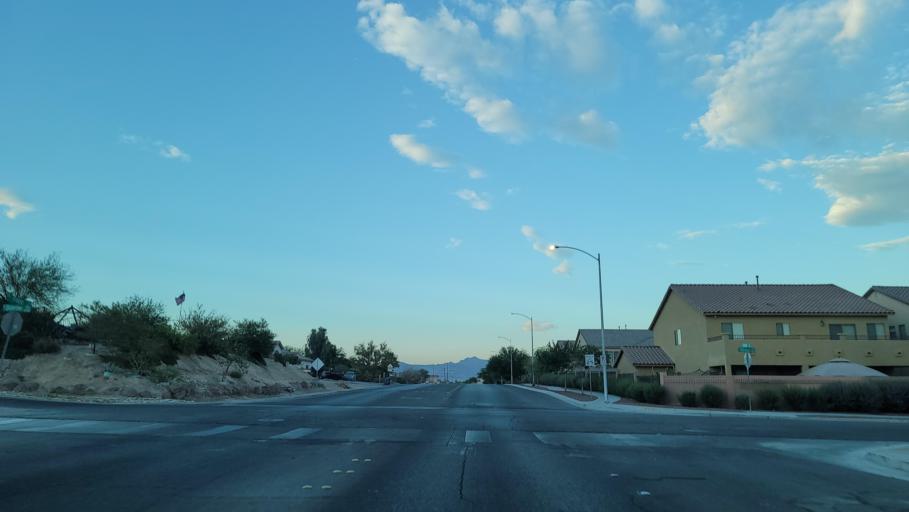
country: US
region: Nevada
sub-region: Clark County
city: Sunrise Manor
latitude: 36.1635
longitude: -115.0353
